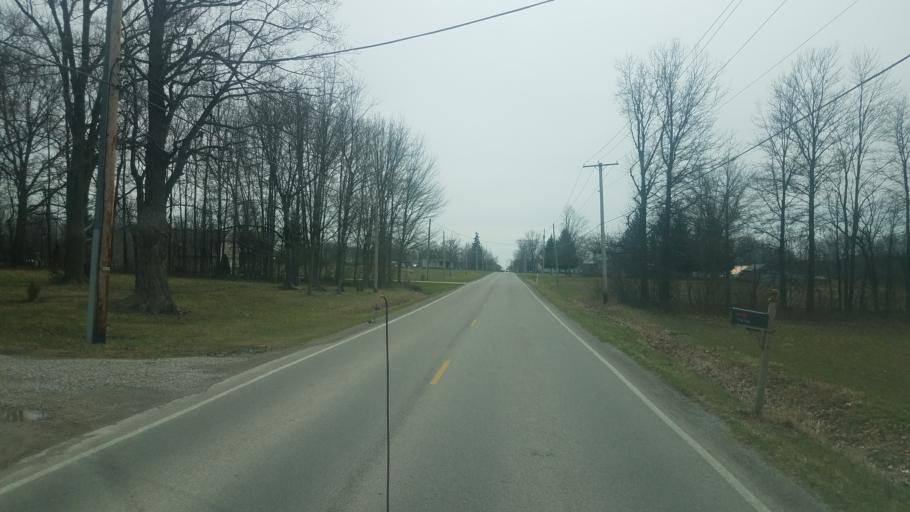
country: US
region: Ohio
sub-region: Huron County
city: Wakeman
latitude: 41.2646
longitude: -82.4917
